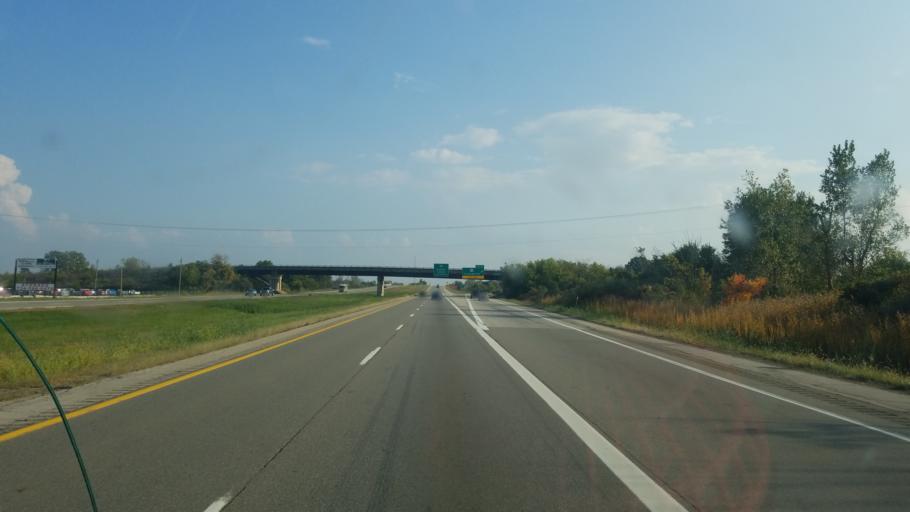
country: US
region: Michigan
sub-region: Monroe County
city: Carleton
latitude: 42.0236
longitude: -83.3513
